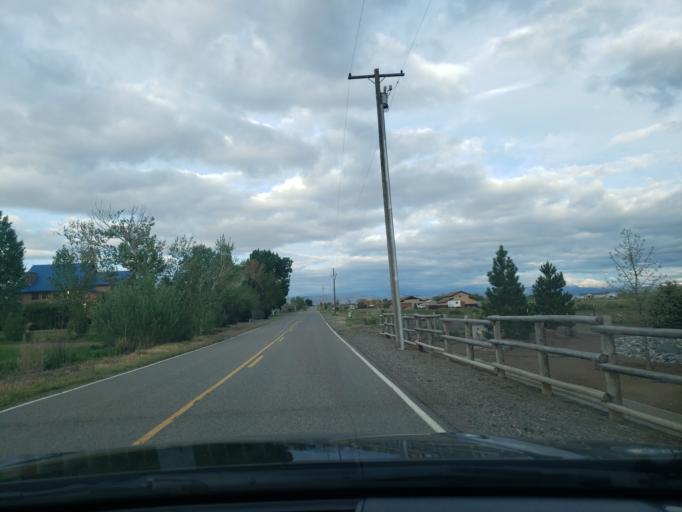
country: US
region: Colorado
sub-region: Mesa County
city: Fruita
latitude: 39.2221
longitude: -108.7183
